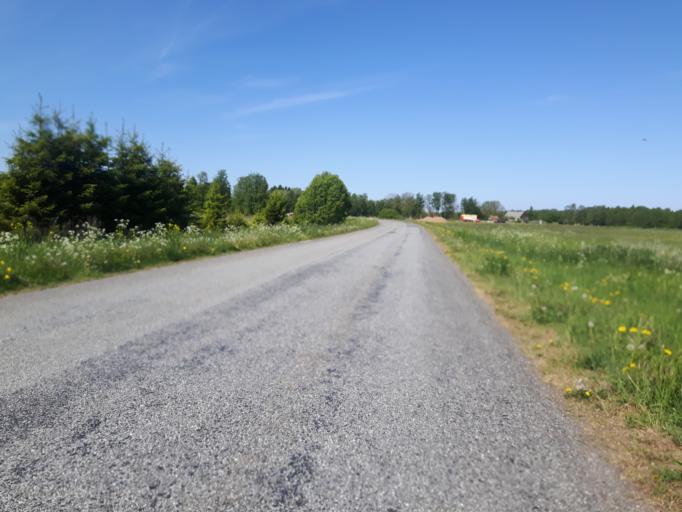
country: EE
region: Ida-Virumaa
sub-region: Aseri vald
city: Aseri
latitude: 59.4736
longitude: 26.8016
